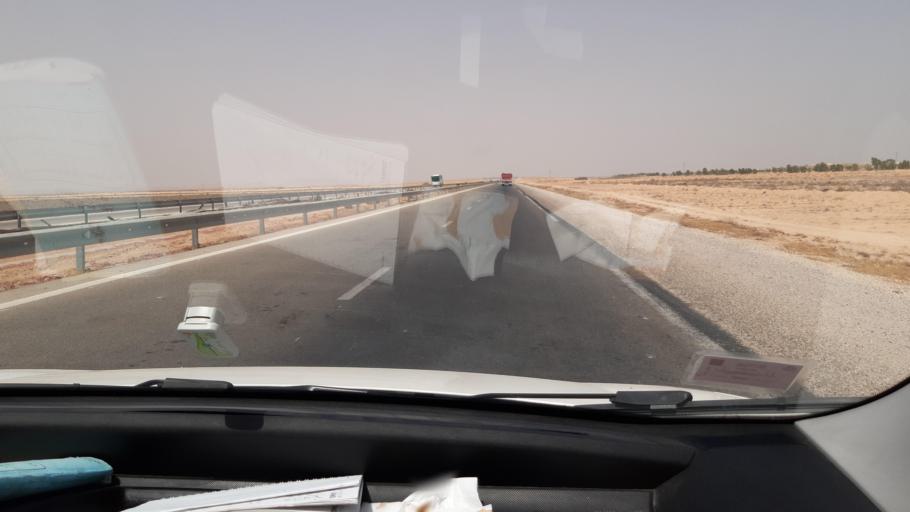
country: TN
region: Qabis
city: Gabes
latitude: 33.9224
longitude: 9.9661
